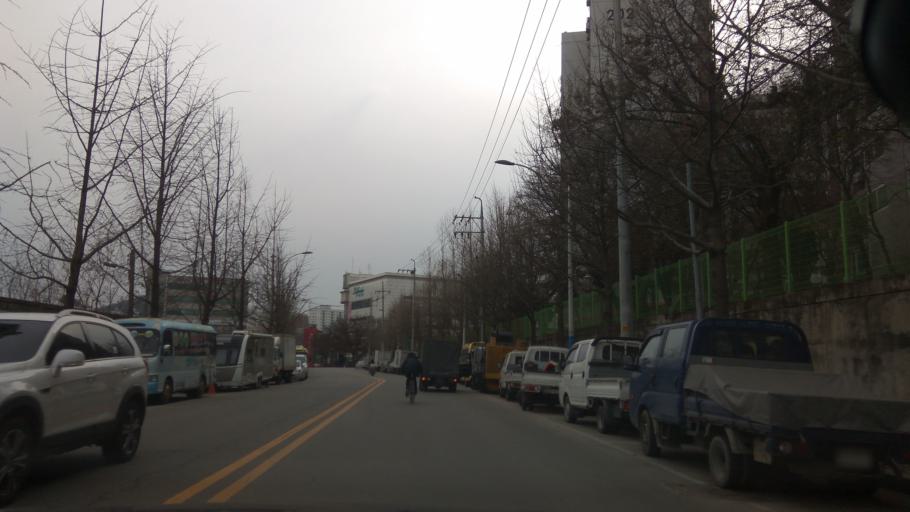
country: KR
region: Incheon
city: Incheon
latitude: 37.4926
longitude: 126.7102
